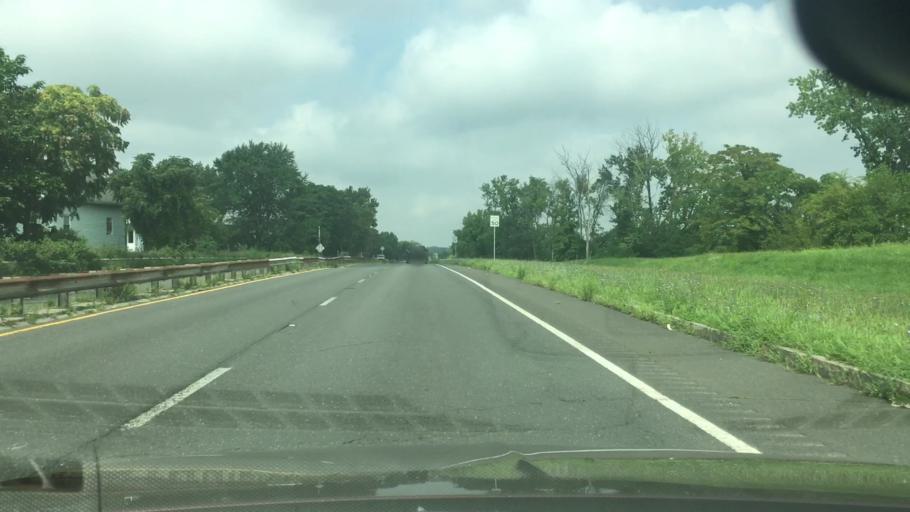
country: US
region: Massachusetts
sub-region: Hampden County
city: Springfield
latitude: 42.1009
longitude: -72.6027
